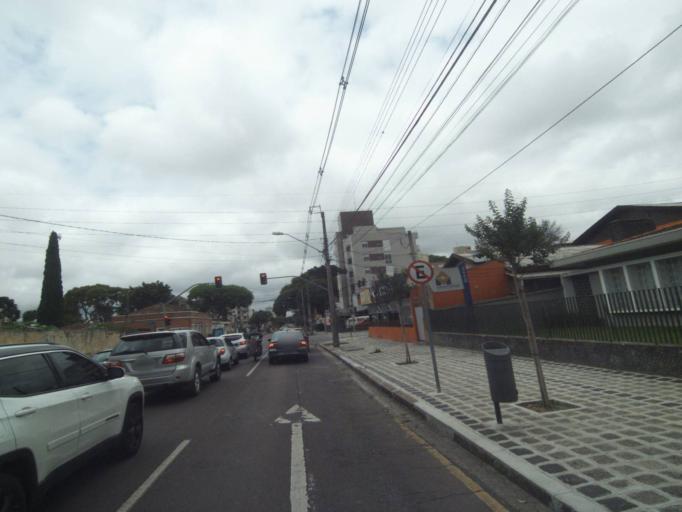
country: BR
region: Parana
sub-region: Curitiba
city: Curitiba
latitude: -25.4269
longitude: -49.2552
